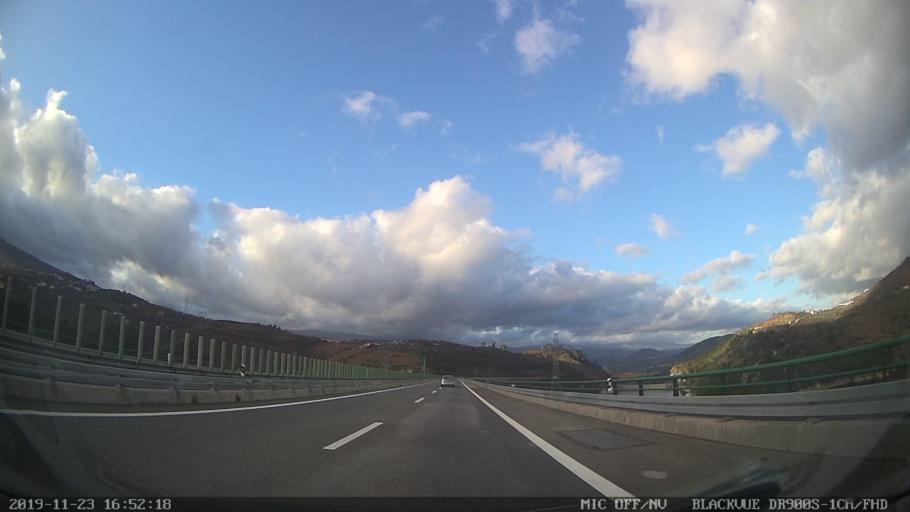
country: PT
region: Viseu
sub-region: Lamego
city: Lamego
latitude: 41.1111
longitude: -7.7766
